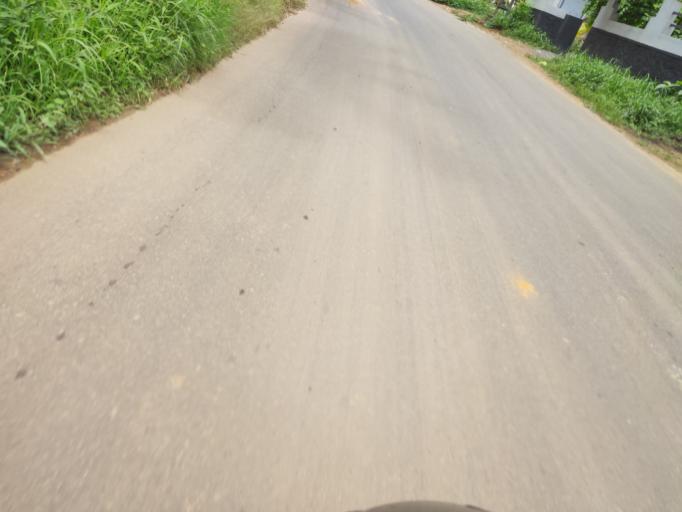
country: IN
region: Kerala
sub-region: Malappuram
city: Manjeri
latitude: 11.2033
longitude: 76.2597
